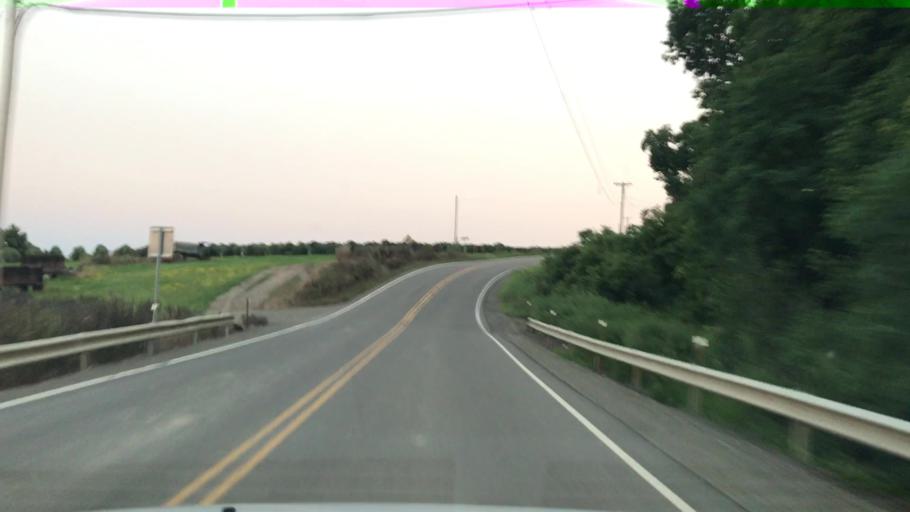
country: US
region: New York
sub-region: Steuben County
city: Sylvan Beach
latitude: 42.5213
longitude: -77.1694
